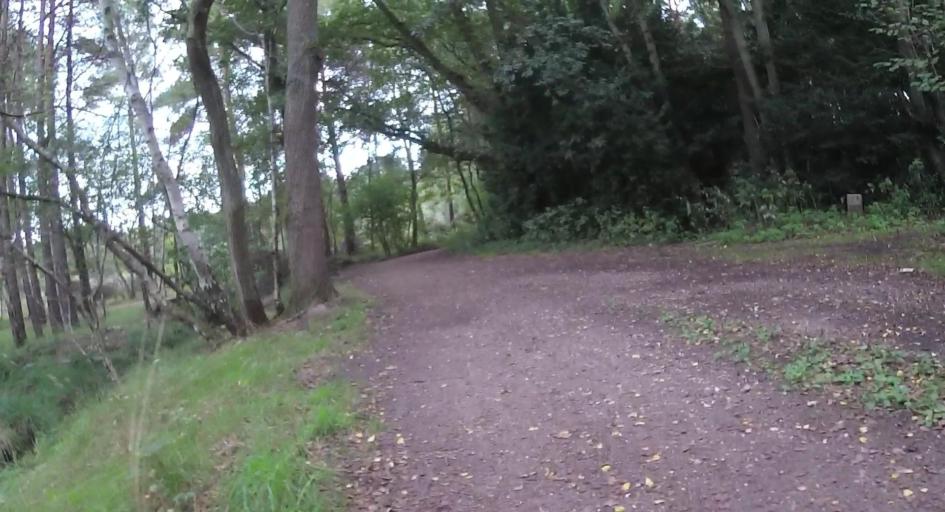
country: GB
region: England
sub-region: Surrey
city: Windlesham
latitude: 51.3387
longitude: -0.6621
